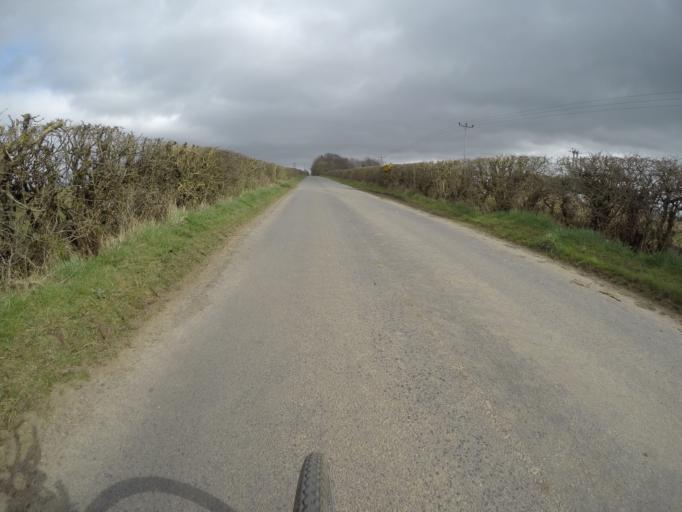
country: GB
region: Scotland
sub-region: East Ayrshire
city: Stewarton
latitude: 55.6747
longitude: -4.5501
